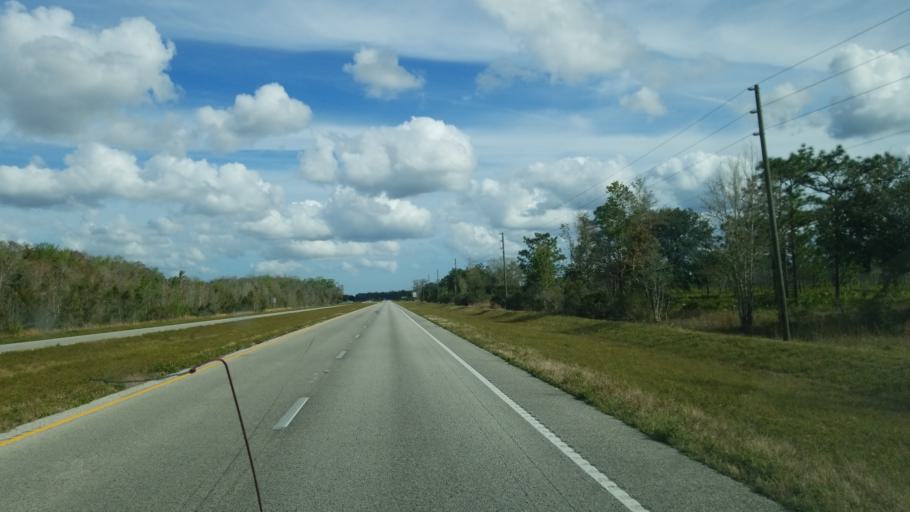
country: US
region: Florida
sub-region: Osceola County
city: Saint Cloud
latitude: 28.1346
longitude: -81.0252
